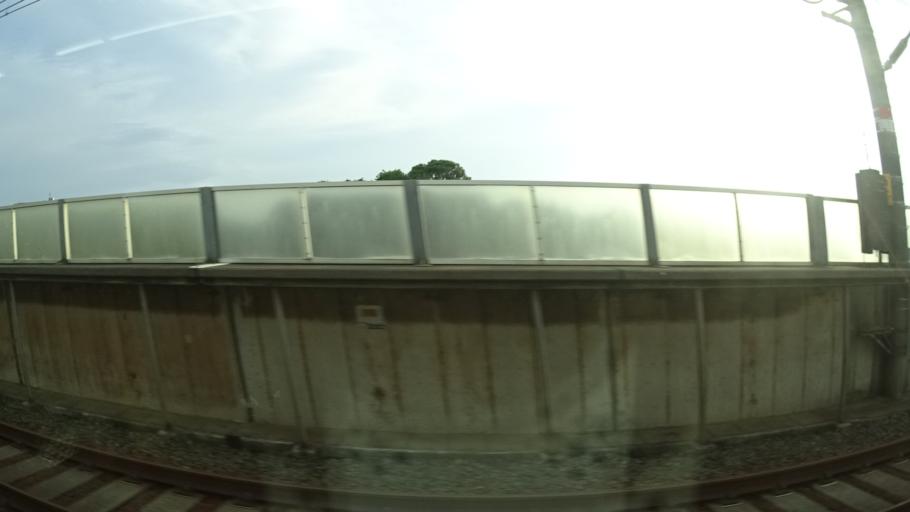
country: JP
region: Saitama
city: Ageoshimo
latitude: 35.9961
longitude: 139.6204
